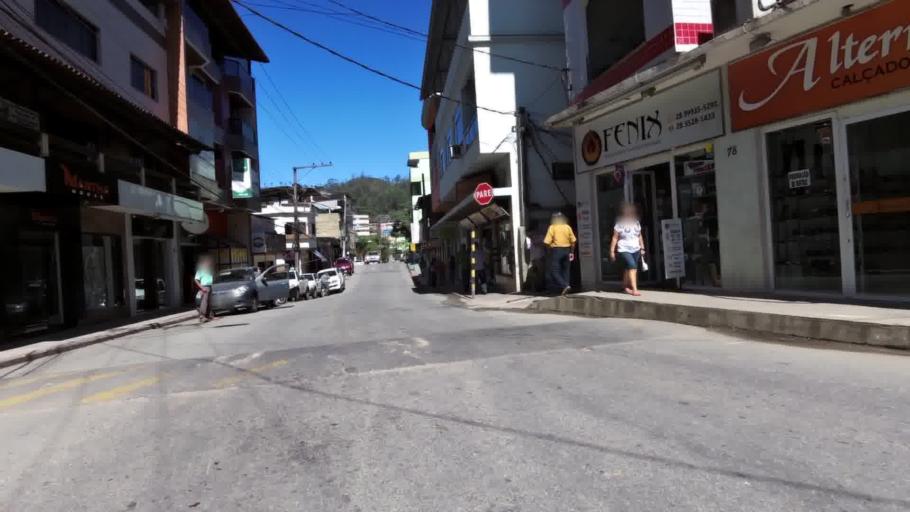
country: BR
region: Espirito Santo
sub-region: Vargem Alta
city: Vargem Alta
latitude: -20.6730
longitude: -41.0099
